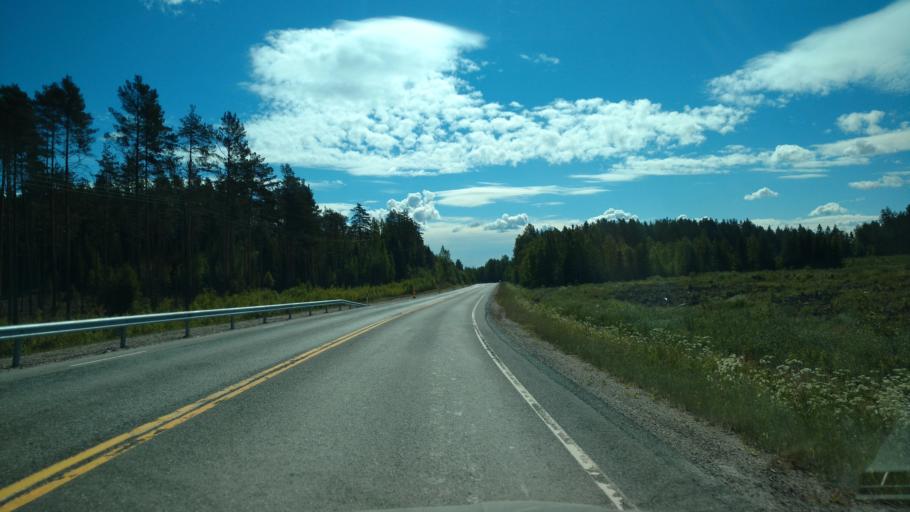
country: FI
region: Varsinais-Suomi
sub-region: Salo
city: Muurla
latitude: 60.3828
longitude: 23.2390
